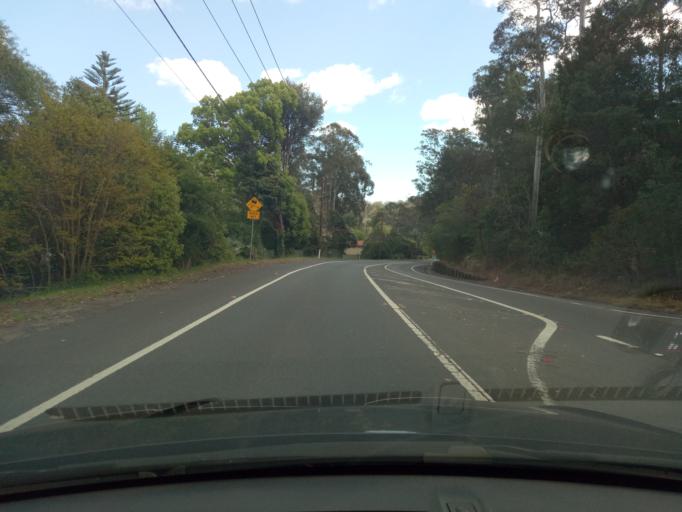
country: AU
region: New South Wales
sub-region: Gosford Shire
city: Lisarow
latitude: -33.3876
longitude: 151.3547
